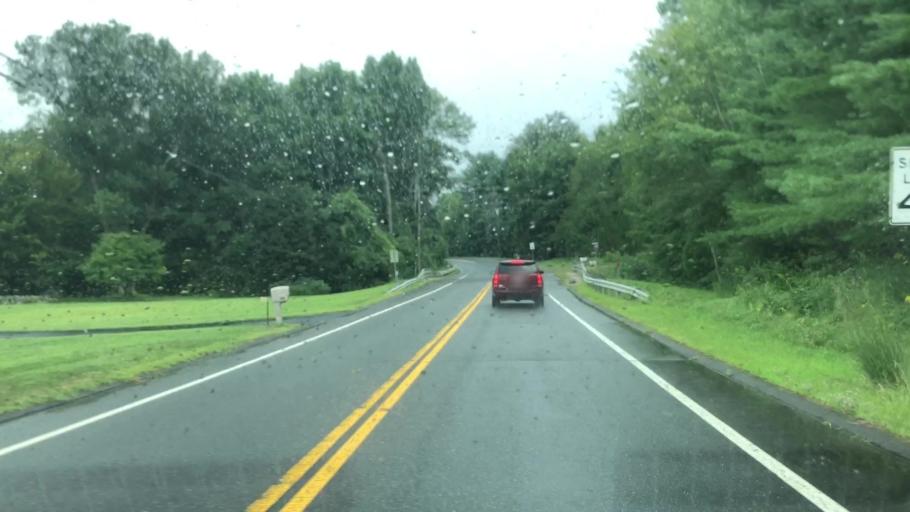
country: US
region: Massachusetts
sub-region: Hampshire County
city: Westhampton
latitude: 42.2838
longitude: -72.7791
